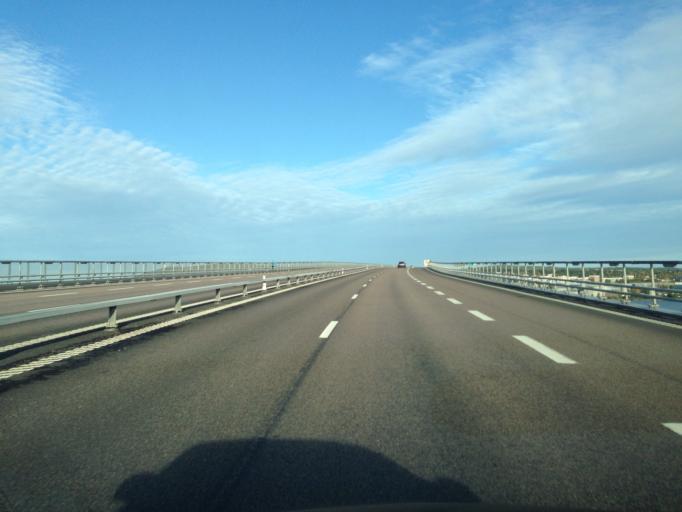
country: SE
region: Vaesternorrland
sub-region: Sundsvalls Kommun
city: Sundsvall
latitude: 62.3841
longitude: 17.3476
